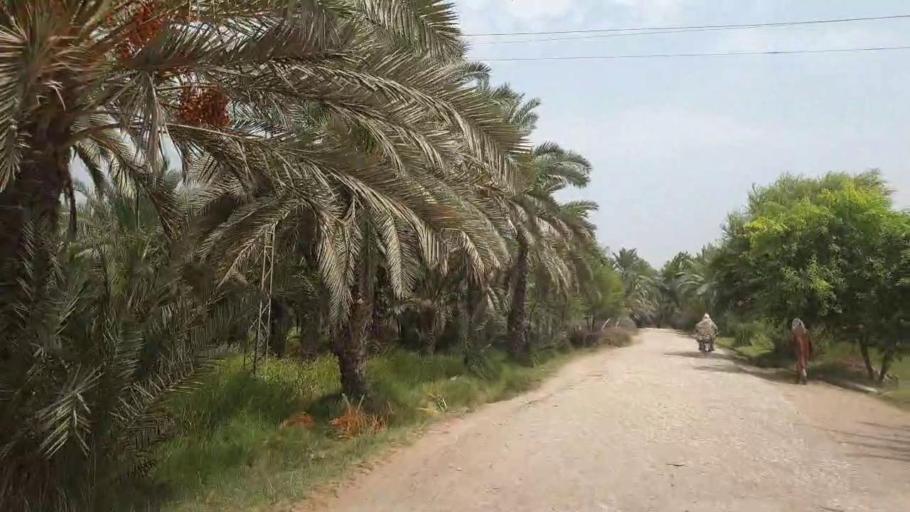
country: PK
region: Sindh
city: Pir jo Goth
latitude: 27.5190
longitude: 68.5790
